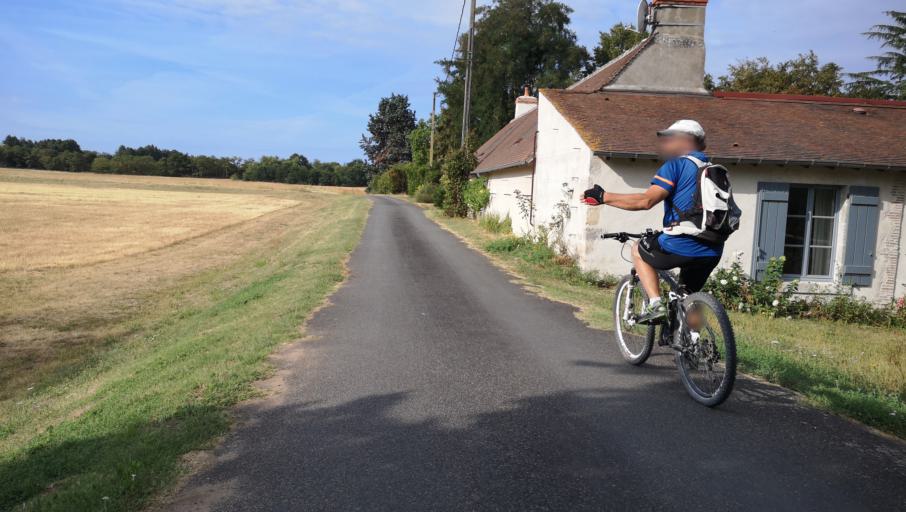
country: FR
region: Centre
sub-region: Departement du Loiret
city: Sandillon
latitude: 47.8656
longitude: 2.0397
